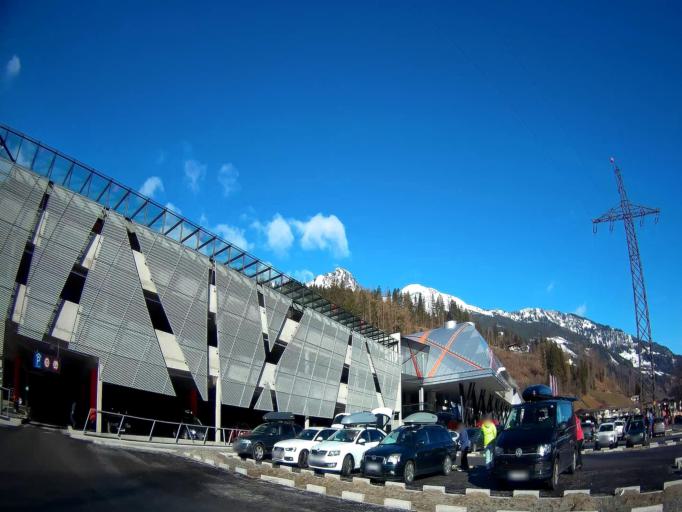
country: AT
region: Salzburg
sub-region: Politischer Bezirk Sankt Johann im Pongau
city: Bad Hofgastein
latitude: 47.1663
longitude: 13.0987
